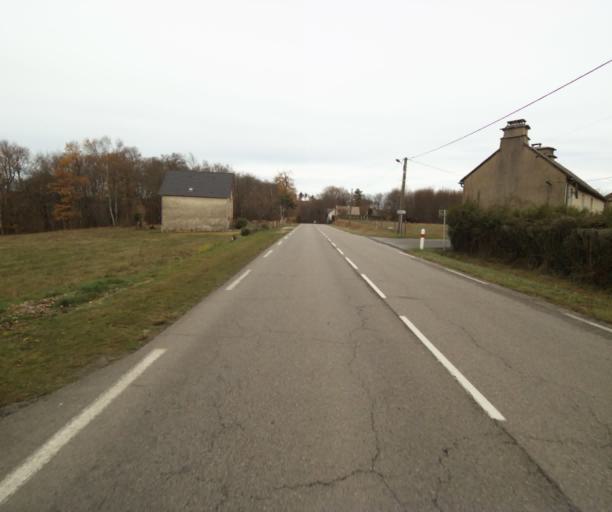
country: FR
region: Limousin
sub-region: Departement de la Correze
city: Sainte-Fortunade
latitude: 45.1783
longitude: 1.7591
